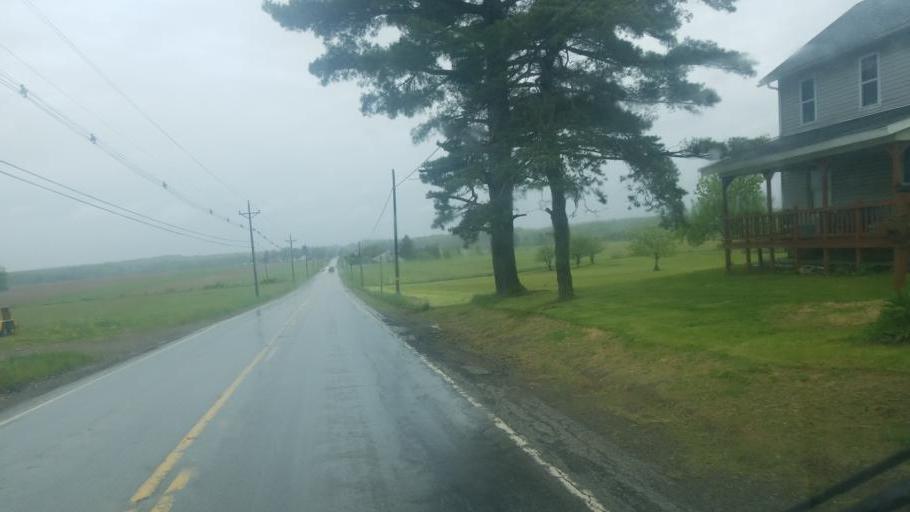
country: US
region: Pennsylvania
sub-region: Forest County
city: Tionesta
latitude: 41.3952
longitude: -79.3347
